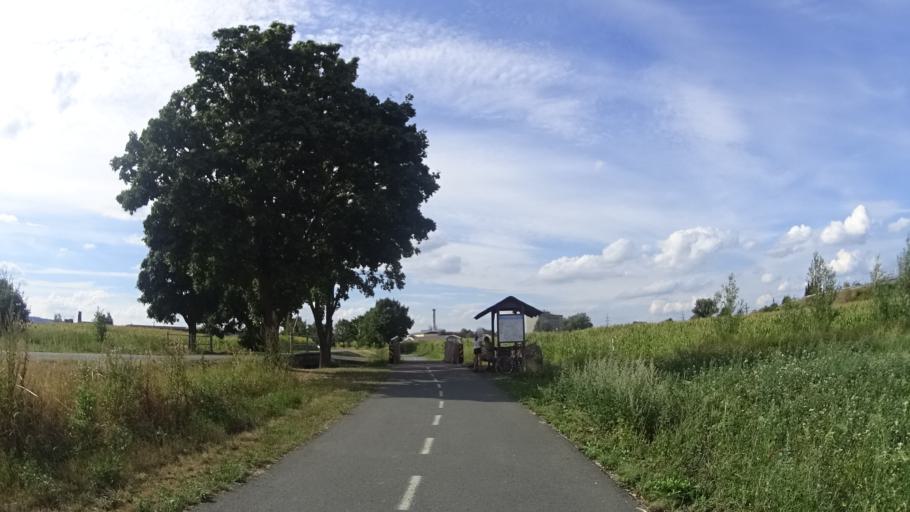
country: CZ
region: Olomoucky
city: Moravicany
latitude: 49.7690
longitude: 16.9460
